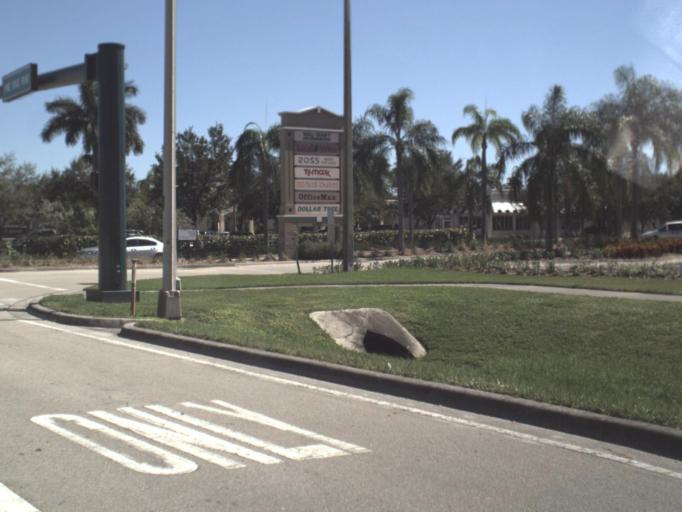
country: US
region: Florida
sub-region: Collier County
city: Pine Ridge
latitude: 26.2116
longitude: -81.7657
